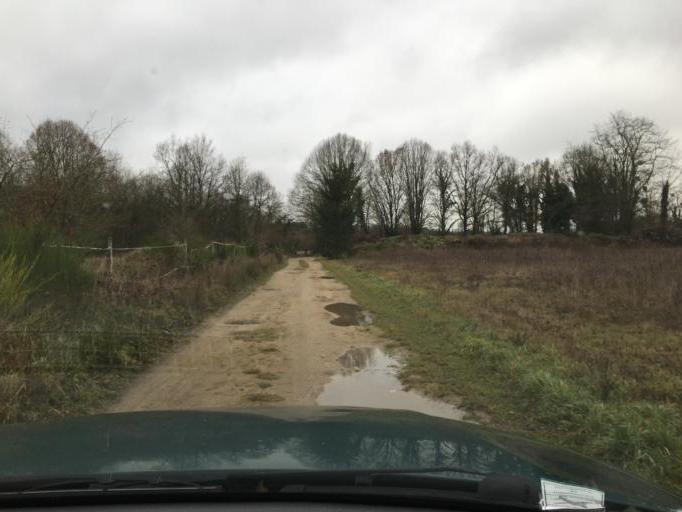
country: FR
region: Centre
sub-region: Departement du Loiret
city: Olivet
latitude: 47.8509
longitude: 1.8785
